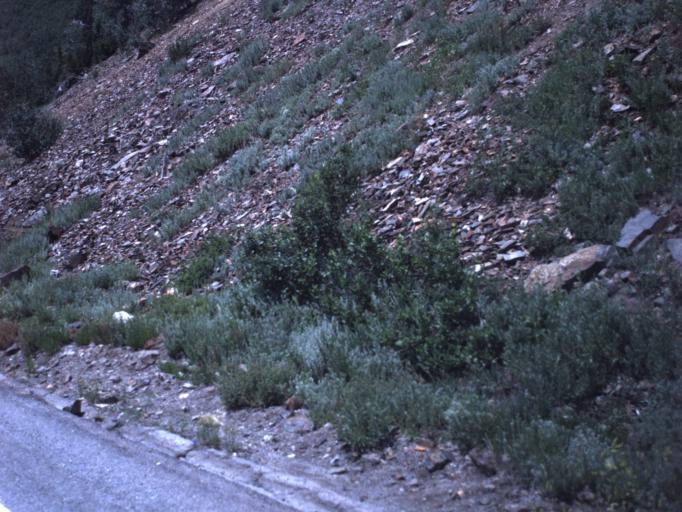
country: US
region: Utah
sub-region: Summit County
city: Snyderville
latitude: 40.5897
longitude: -111.6399
